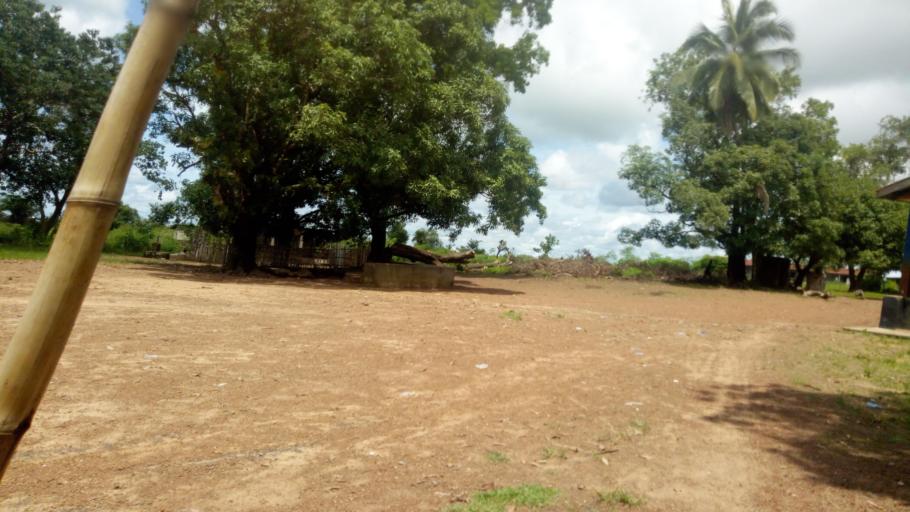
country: SL
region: Northern Province
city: Magburaka
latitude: 8.7136
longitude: -11.9541
